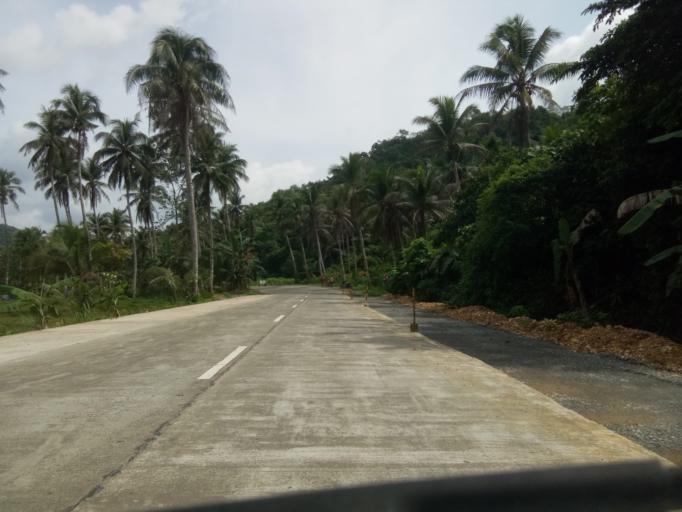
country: PH
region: Caraga
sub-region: Province of Surigao del Norte
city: Dapa
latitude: 9.8006
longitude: 126.0662
